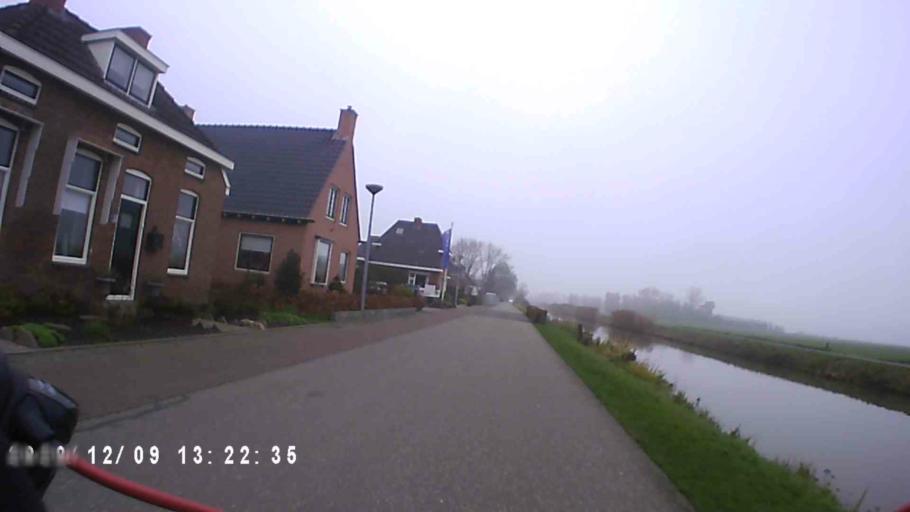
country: NL
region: Groningen
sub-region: Gemeente Bedum
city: Bedum
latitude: 53.2640
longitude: 6.5957
